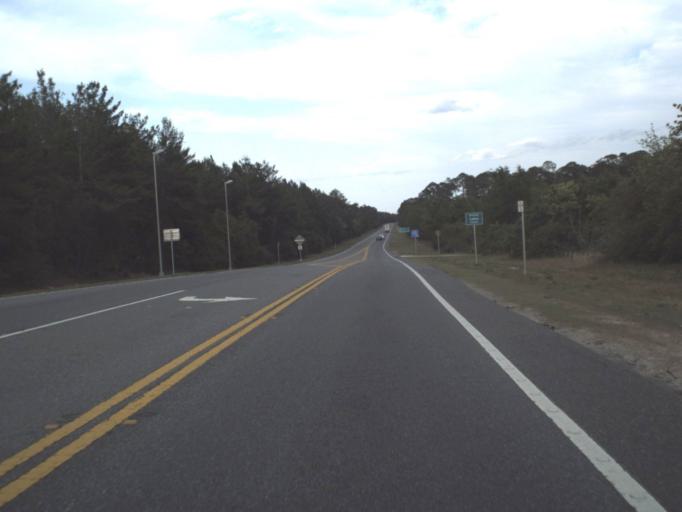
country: US
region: Florida
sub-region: Lake County
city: Astor
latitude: 29.1687
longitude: -81.6415
